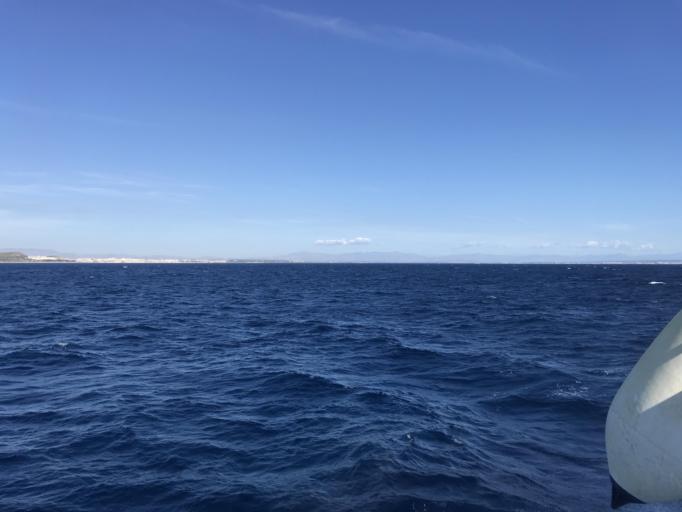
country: ES
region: Valencia
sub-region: Provincia de Alicante
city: Guardamar del Segura
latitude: 38.0303
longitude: -0.6152
